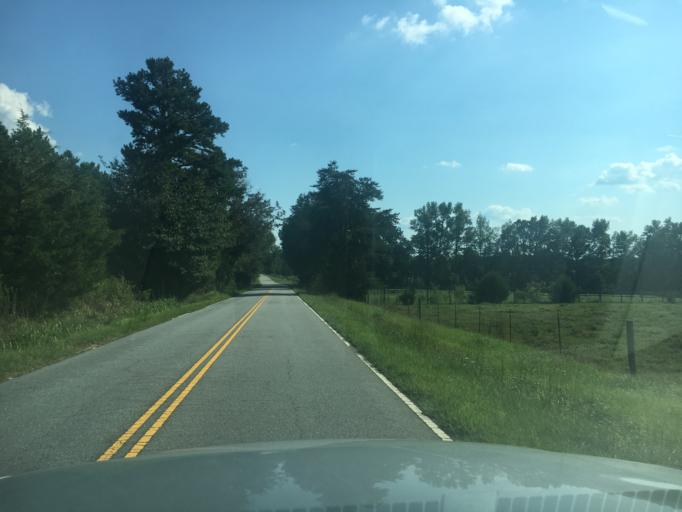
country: US
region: South Carolina
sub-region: Pickens County
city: Liberty
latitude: 34.7298
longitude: -82.6403
